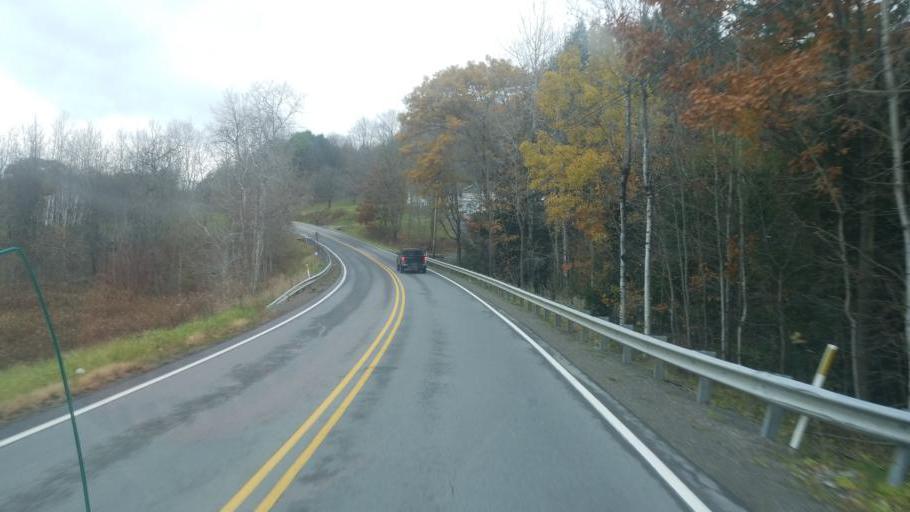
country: US
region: Pennsylvania
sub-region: Elk County
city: Ridgway
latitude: 41.3115
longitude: -78.6594
